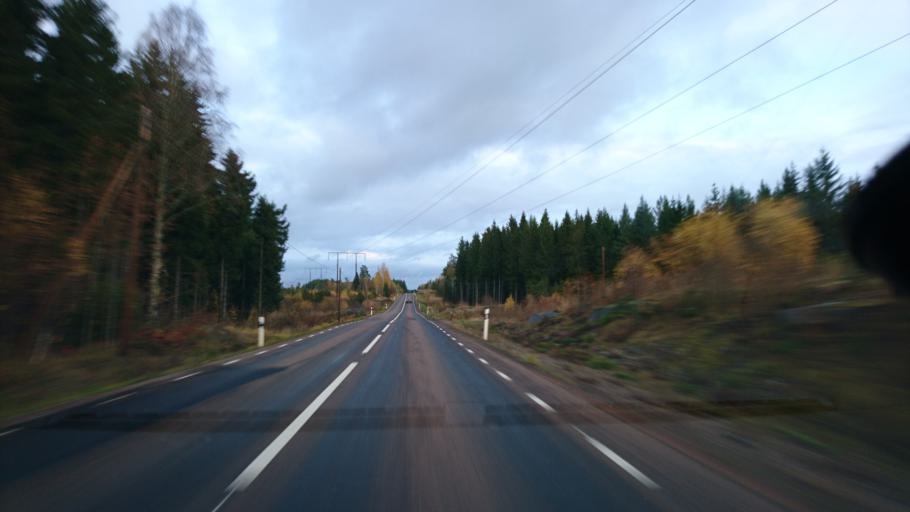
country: SE
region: Uppsala
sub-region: Osthammars Kommun
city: Gimo
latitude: 59.9821
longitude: 18.2085
